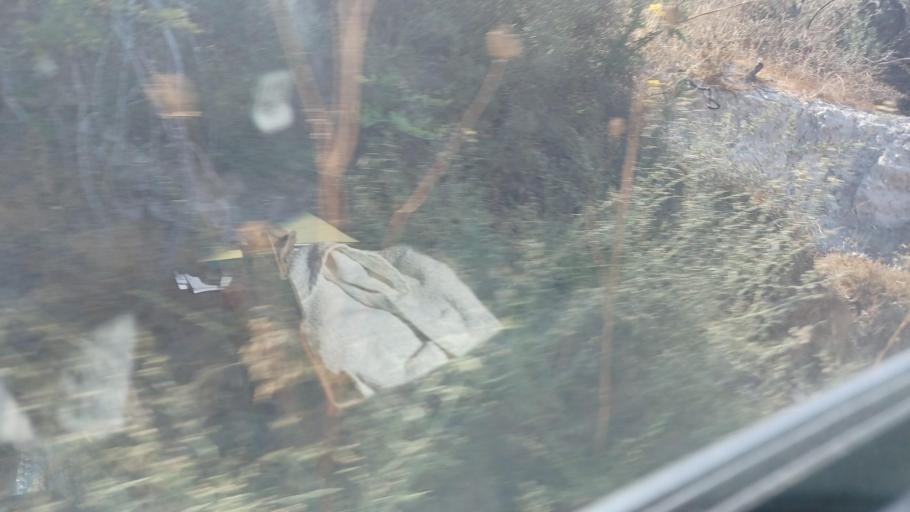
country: CY
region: Pafos
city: Mesogi
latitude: 34.8807
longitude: 32.5350
